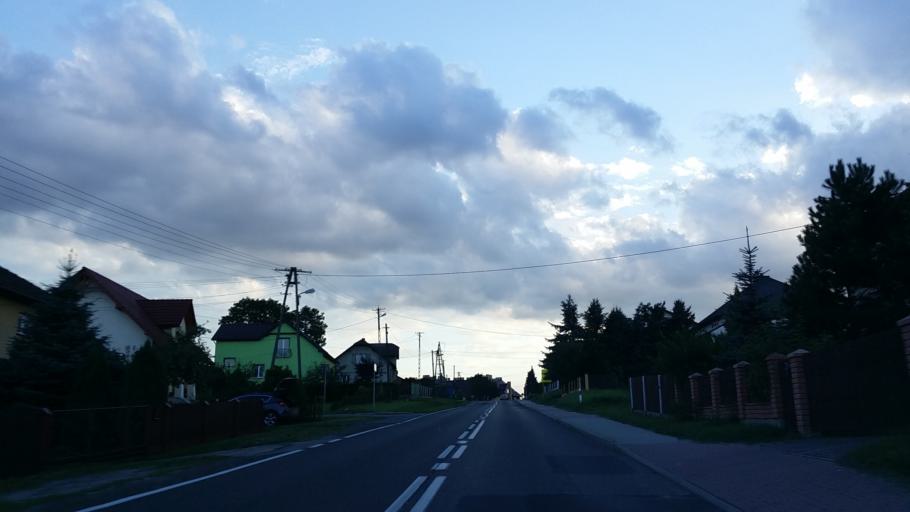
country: PL
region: Lesser Poland Voivodeship
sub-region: Powiat oswiecimski
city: Polanka Wielka
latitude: 49.9784
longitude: 19.2954
